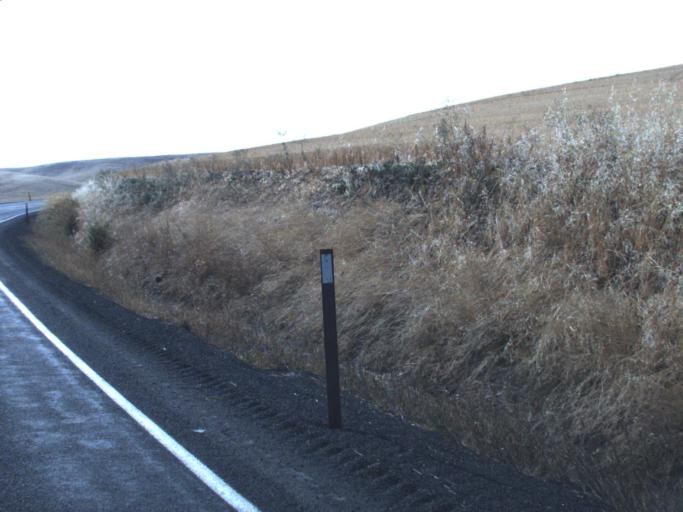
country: US
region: Idaho
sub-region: Latah County
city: Moscow
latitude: 46.9587
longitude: -117.0900
